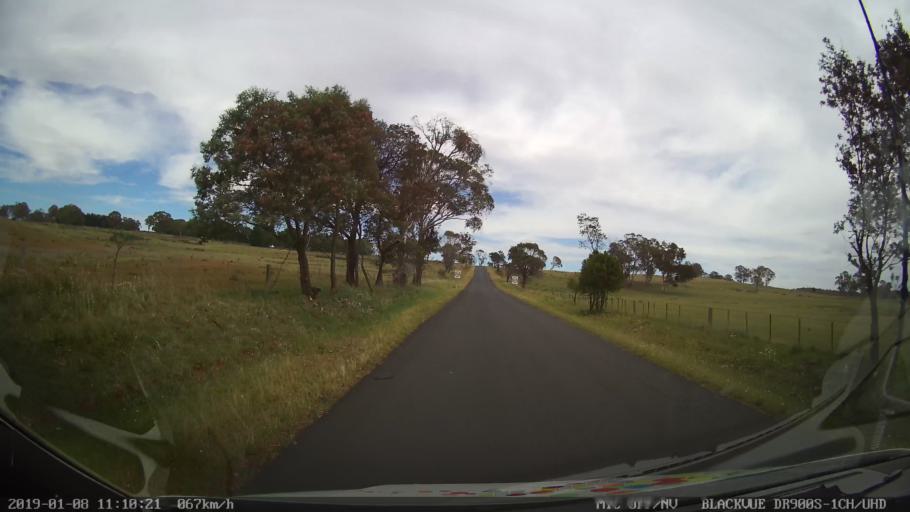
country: AU
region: New South Wales
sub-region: Guyra
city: Guyra
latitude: -30.2259
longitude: 151.6374
